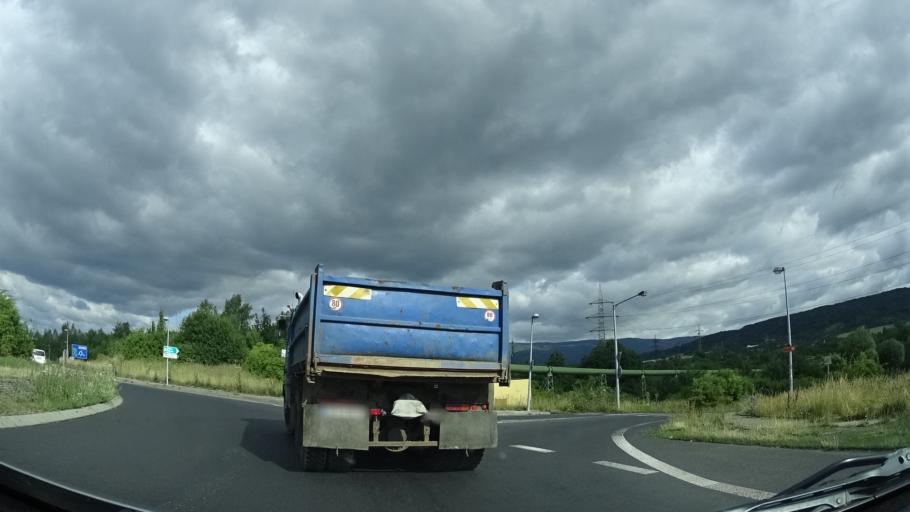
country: CZ
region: Ustecky
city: Trmice
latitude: 50.6485
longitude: 13.9969
